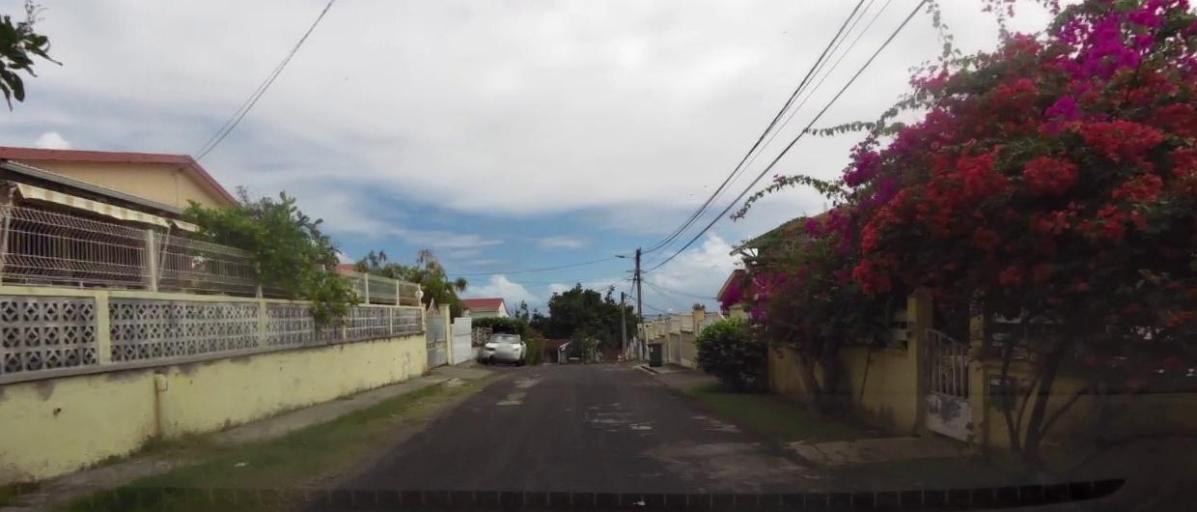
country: GP
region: Guadeloupe
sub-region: Guadeloupe
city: Petit-Bourg
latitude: 16.1977
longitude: -61.5907
